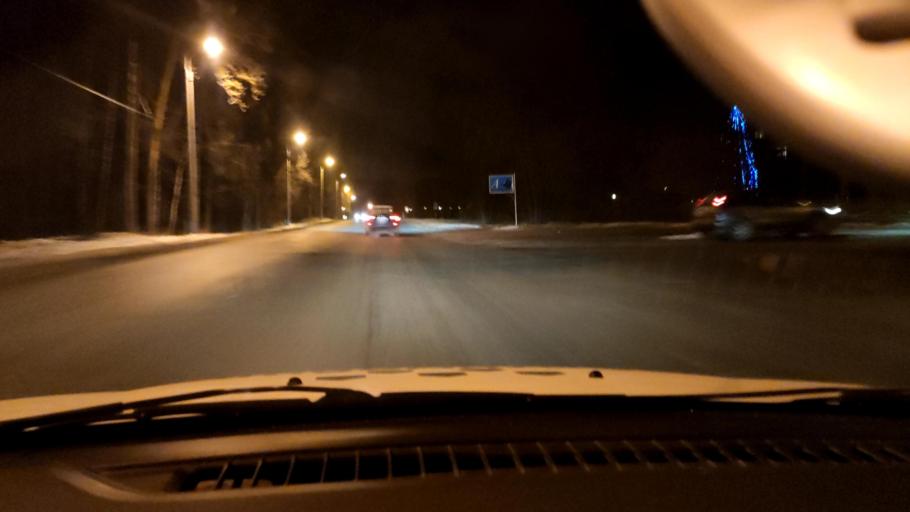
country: RU
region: Perm
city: Kultayevo
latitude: 58.0113
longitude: 55.9818
